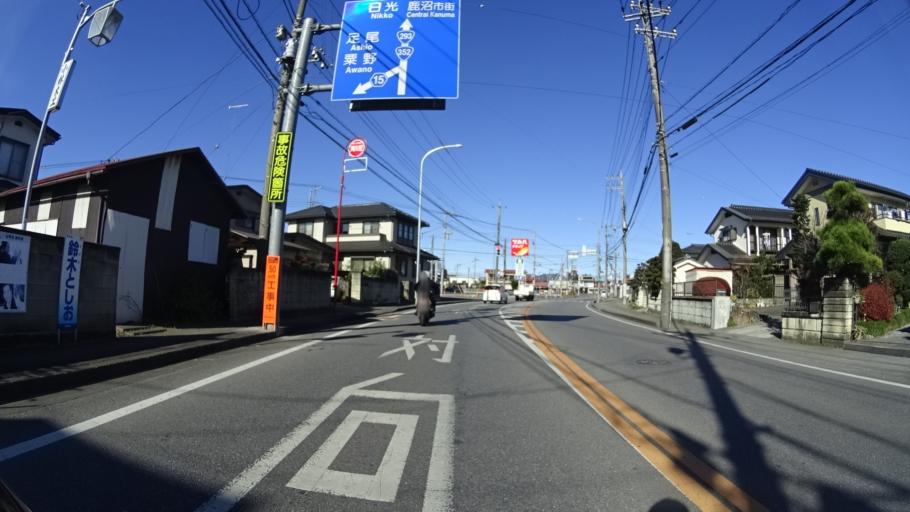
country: JP
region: Tochigi
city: Kanuma
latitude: 36.5388
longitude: 139.7470
